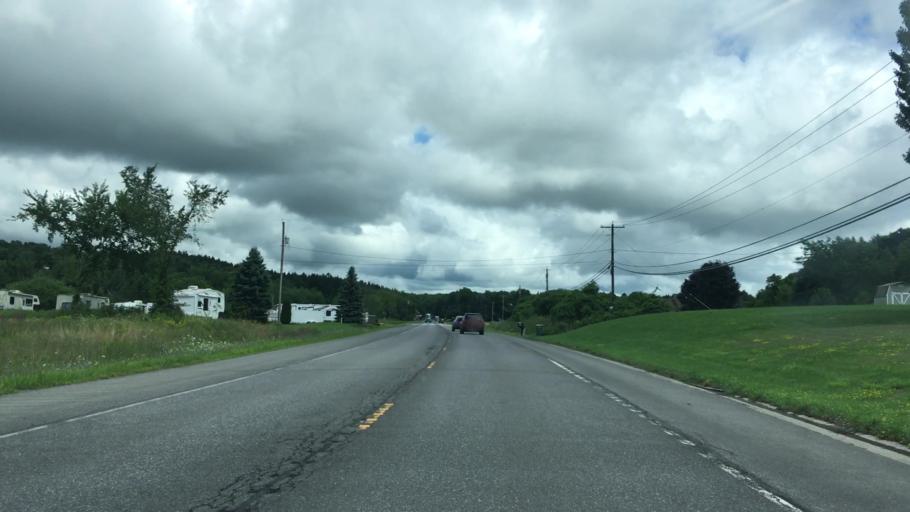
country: US
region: New York
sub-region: Rensselaer County
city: Poestenkill
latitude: 42.7842
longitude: -73.5768
